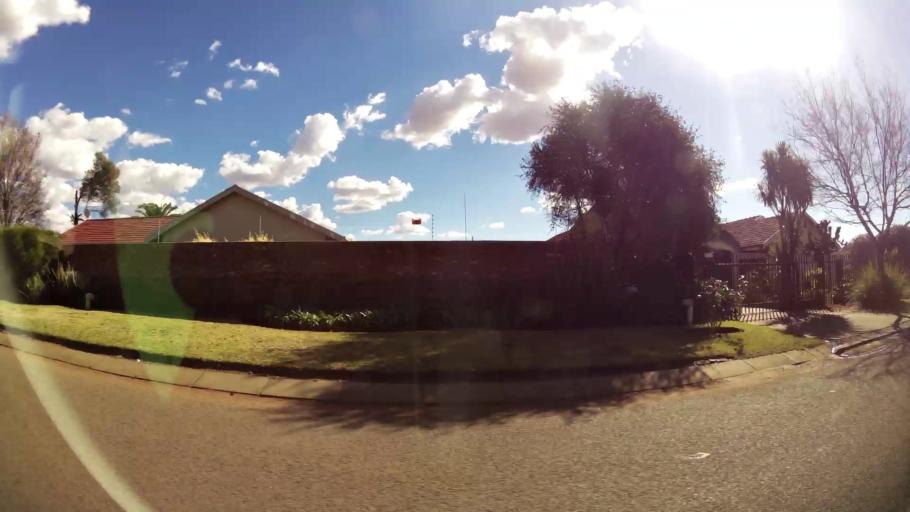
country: ZA
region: North-West
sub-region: Dr Kenneth Kaunda District Municipality
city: Klerksdorp
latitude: -26.8642
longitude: 26.6191
